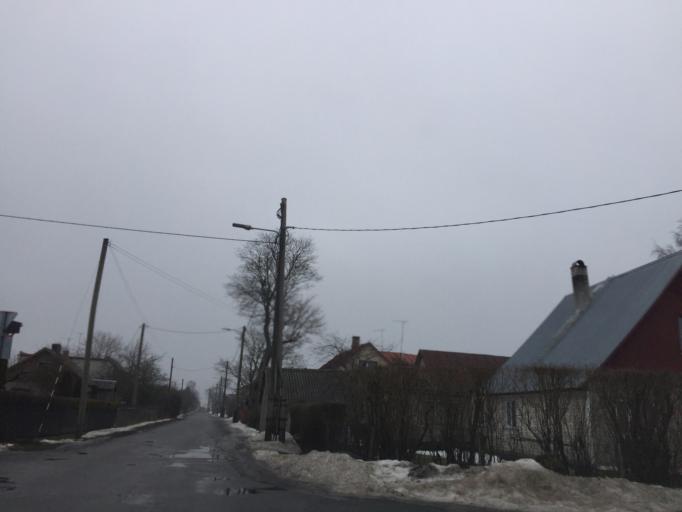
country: EE
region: Saare
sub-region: Kuressaare linn
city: Kuressaare
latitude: 58.2472
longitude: 22.4899
